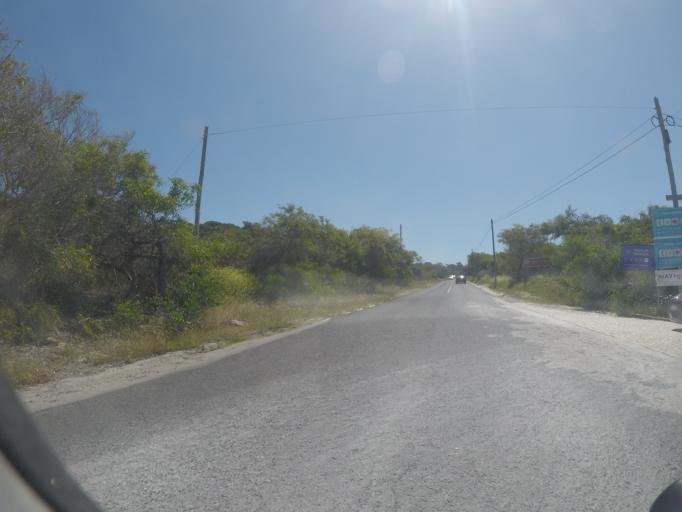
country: PT
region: Setubal
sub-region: Almada
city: Charneca
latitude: 38.6095
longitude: -9.2061
